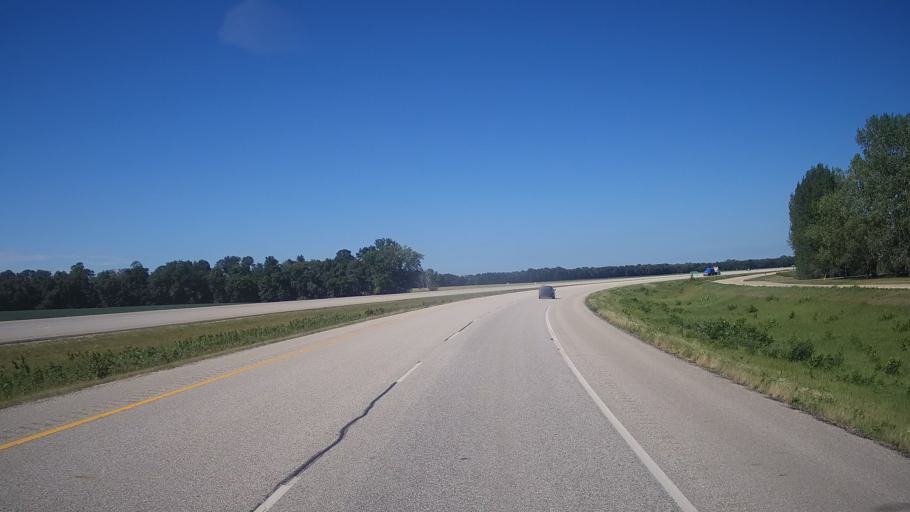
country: CA
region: Manitoba
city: Portage la Prairie
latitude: 49.9468
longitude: -98.2937
